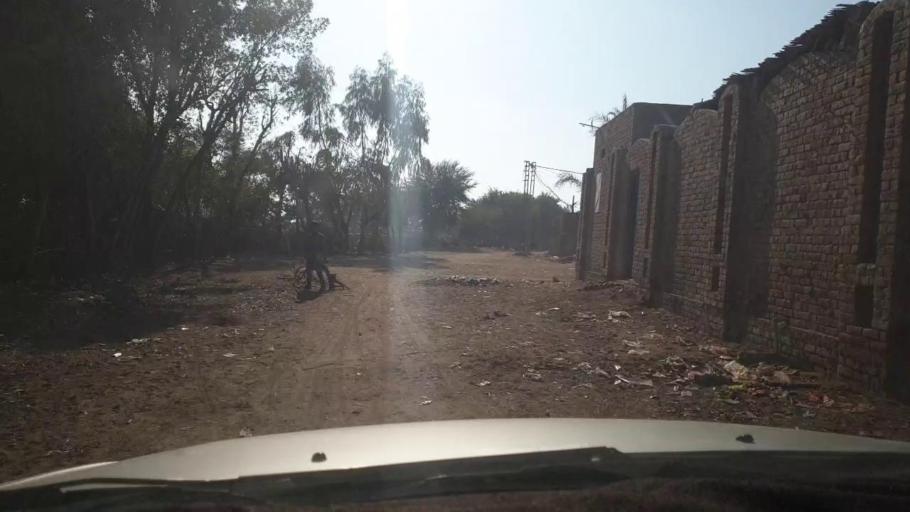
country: PK
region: Sindh
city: Mirpur Mathelo
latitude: 27.9821
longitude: 69.5398
